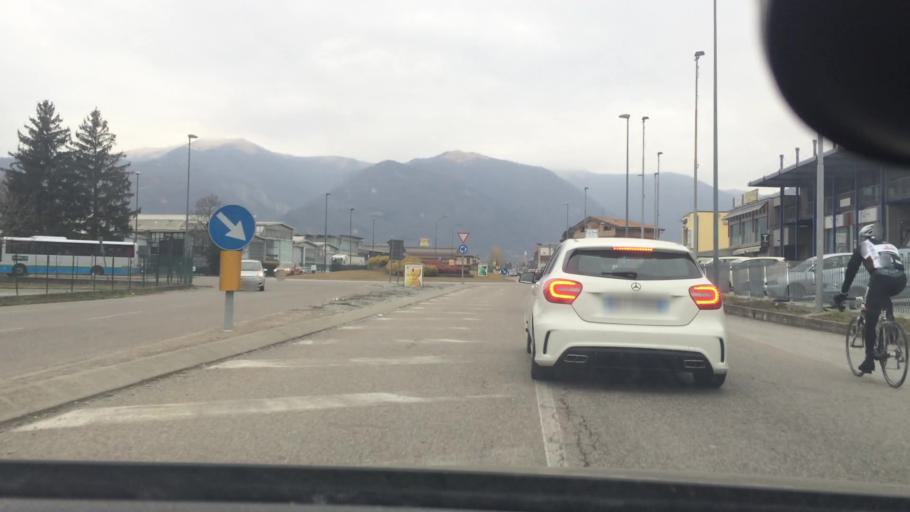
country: IT
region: Lombardy
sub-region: Provincia di Como
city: Merone
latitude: 45.7946
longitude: 9.2421
